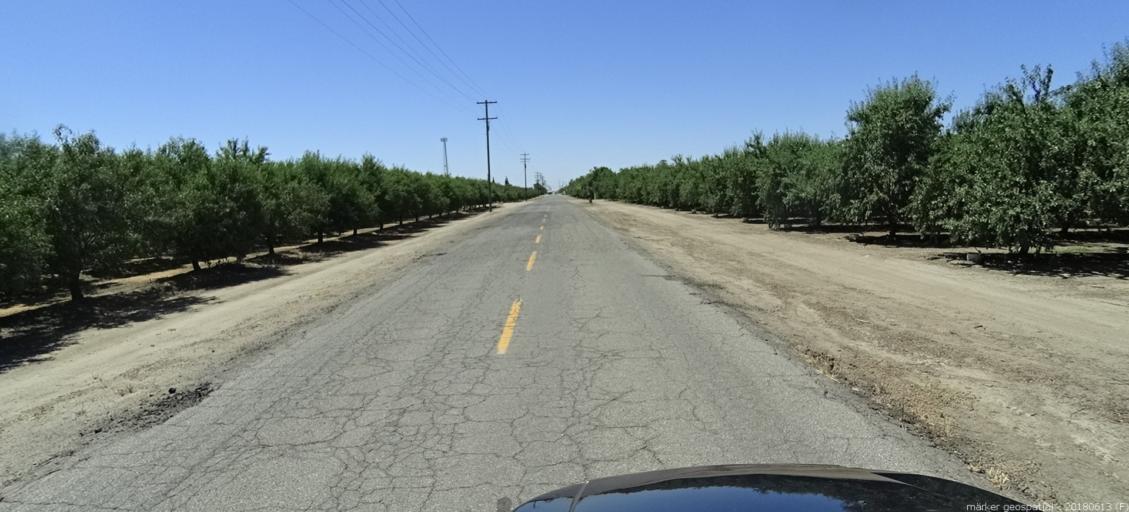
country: US
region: California
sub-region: Madera County
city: Chowchilla
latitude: 37.0230
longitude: -120.3105
